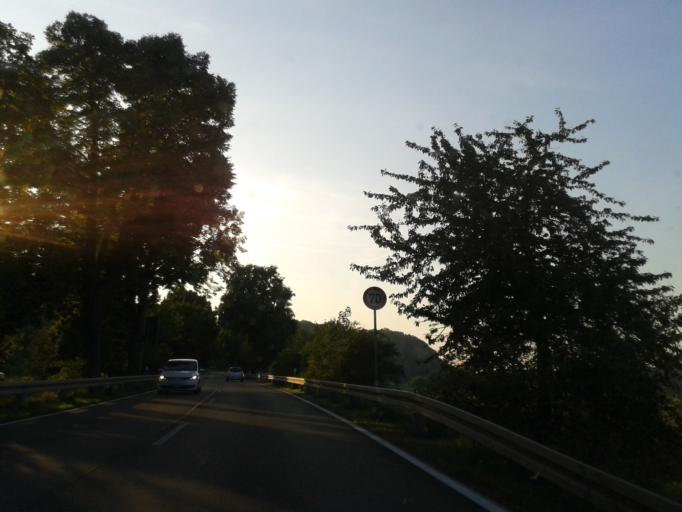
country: DE
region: Saxony
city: Meissen
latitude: 51.1713
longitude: 13.4688
